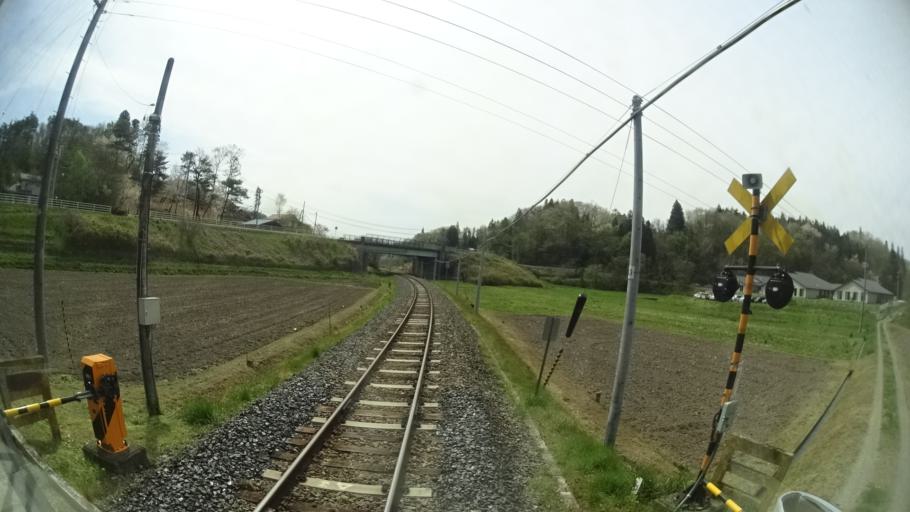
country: JP
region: Iwate
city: Ichinoseki
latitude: 38.9407
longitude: 141.3389
